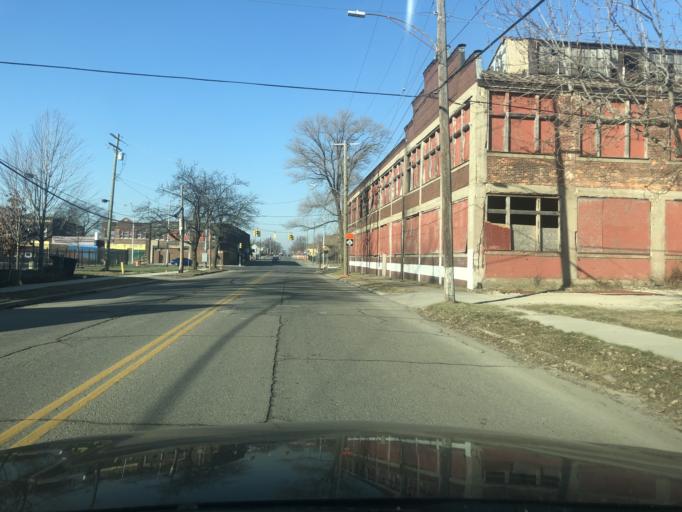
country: US
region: Michigan
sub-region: Wayne County
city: River Rouge
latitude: 42.3090
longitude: -83.0954
